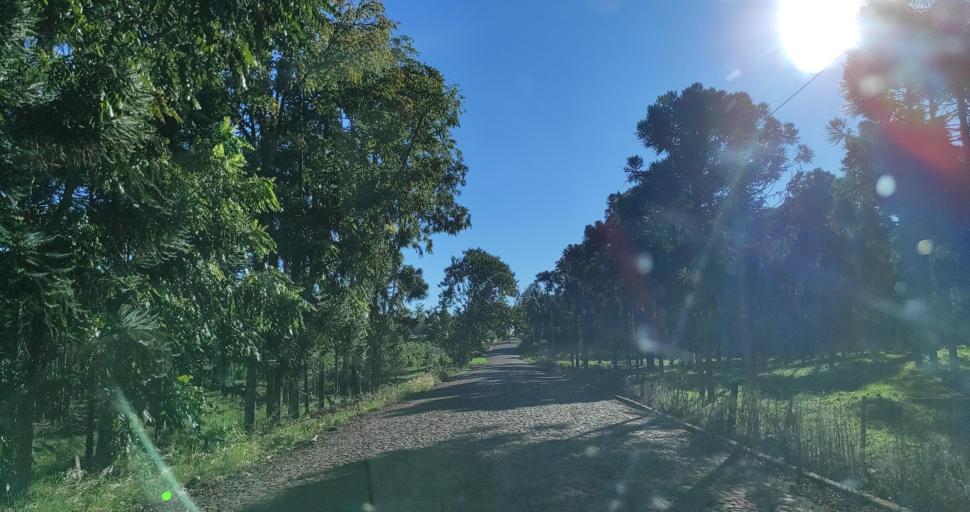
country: AR
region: Misiones
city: Puerto Rico
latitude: -26.8252
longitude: -55.0021
